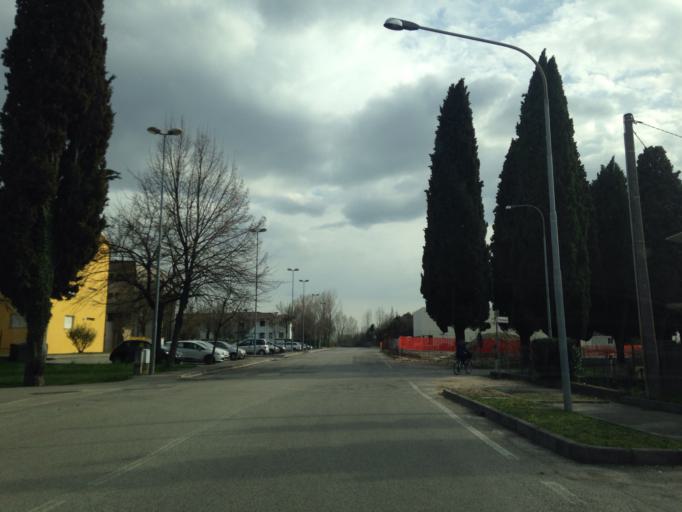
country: IT
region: Friuli Venezia Giulia
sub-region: Provincia di Pordenone
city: Sacile
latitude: 45.9475
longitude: 12.5045
